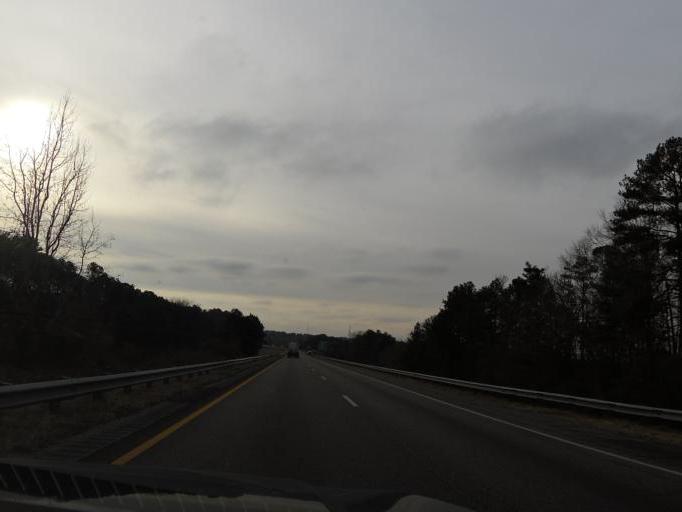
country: US
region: Alabama
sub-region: Autauga County
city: Pine Level
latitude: 32.5609
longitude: -86.4636
